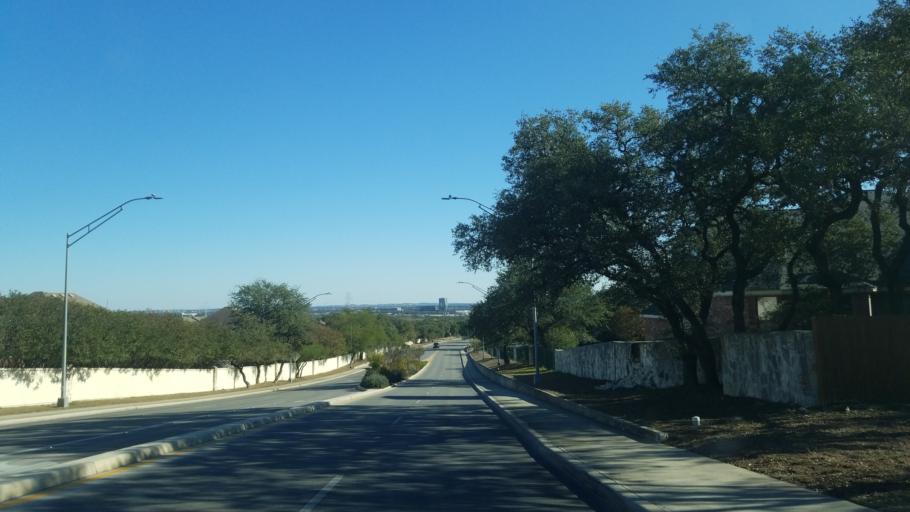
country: US
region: Texas
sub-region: Bexar County
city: Hollywood Park
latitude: 29.6361
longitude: -98.4847
